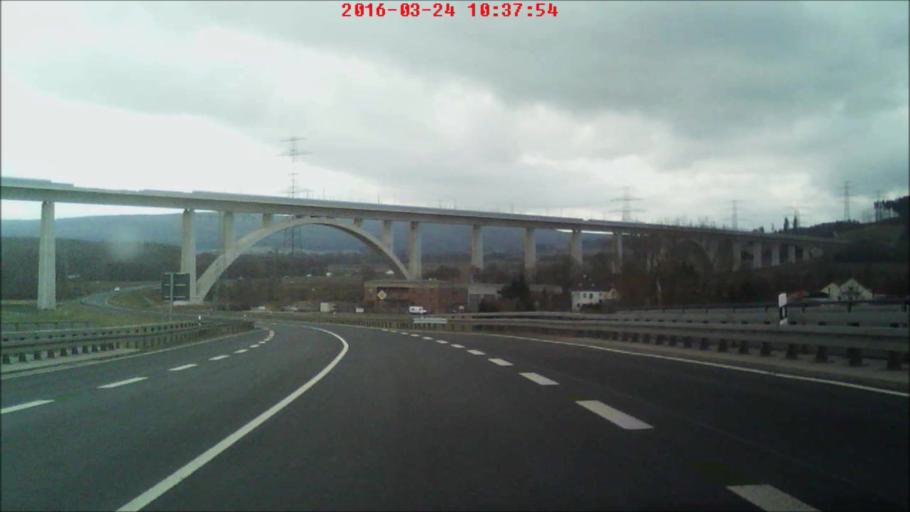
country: DE
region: Thuringia
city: Langewiesen
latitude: 50.6777
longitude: 10.9865
